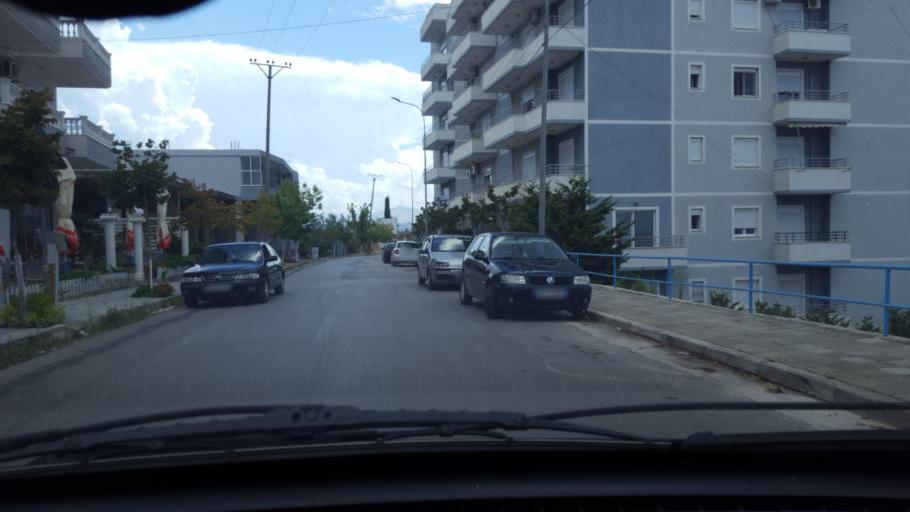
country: AL
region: Vlore
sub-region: Rrethi i Sarandes
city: Sarande
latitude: 39.8495
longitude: 20.0230
